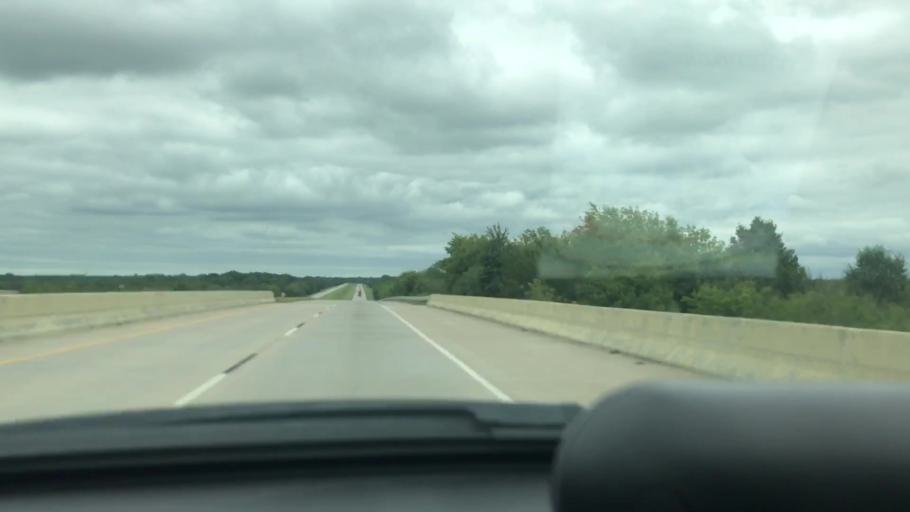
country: US
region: Oklahoma
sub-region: Wagoner County
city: Wagoner
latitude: 35.8865
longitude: -95.4025
